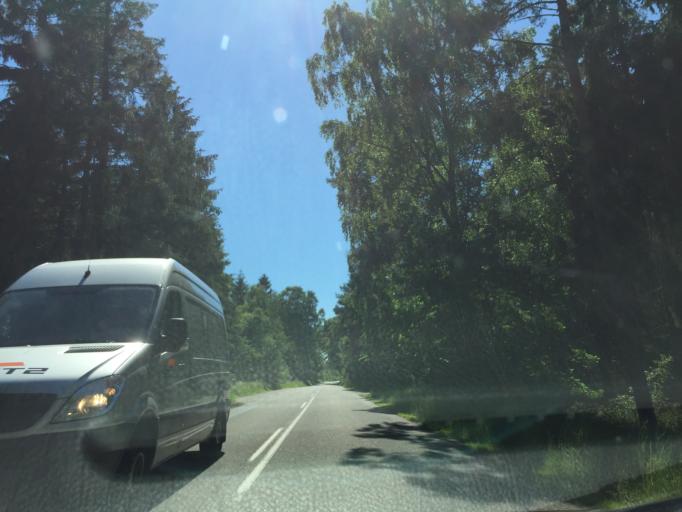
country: DK
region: Central Jutland
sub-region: Viborg Kommune
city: Bjerringbro
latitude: 56.3138
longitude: 9.6063
